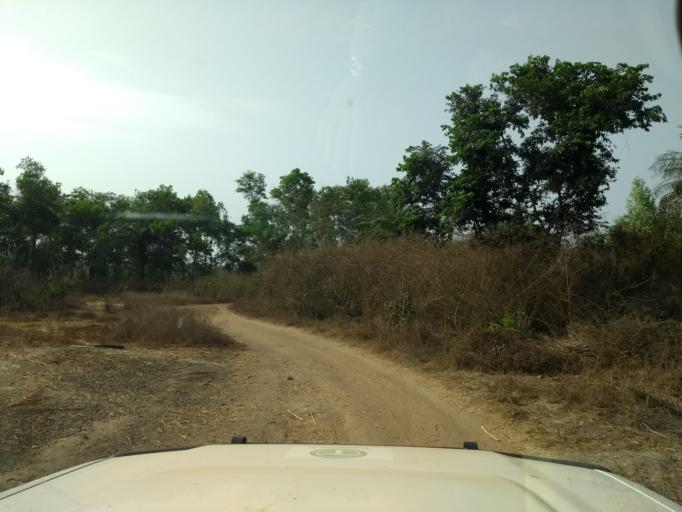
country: GN
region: Kindia
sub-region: Prefecture de Dubreka
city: Dubreka
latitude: 9.8227
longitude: -13.5554
